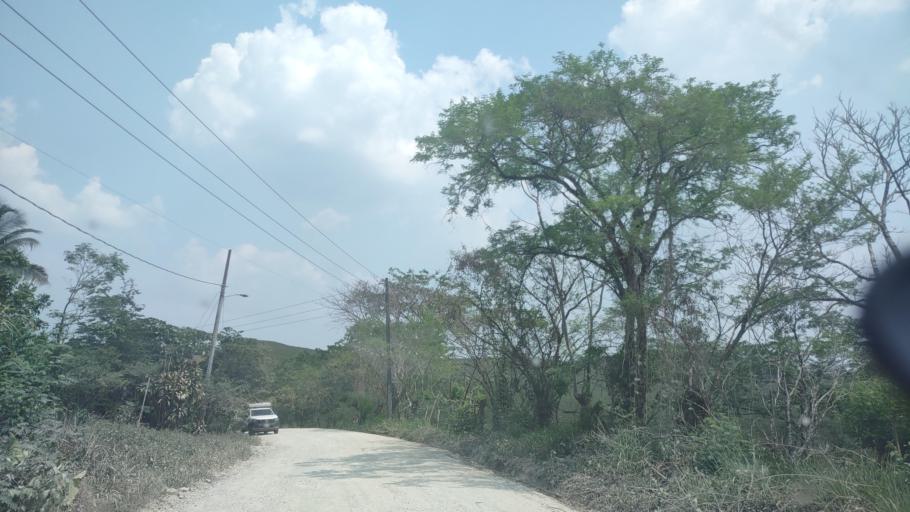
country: MX
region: Tabasco
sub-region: Huimanguillo
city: Francisco Rueda
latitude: 17.6021
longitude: -93.9043
